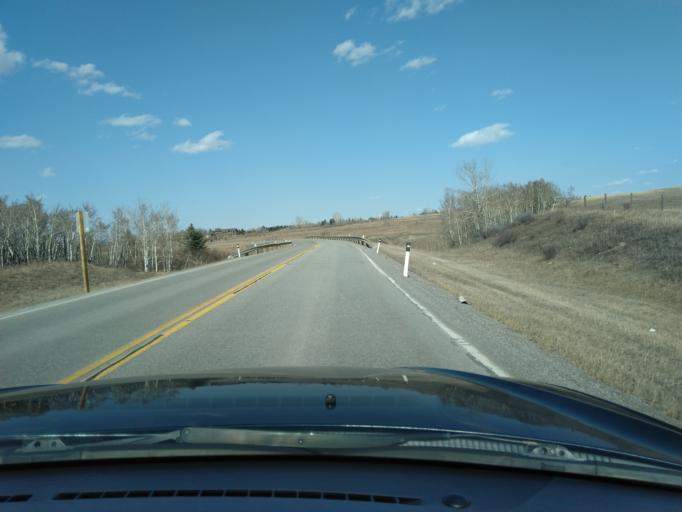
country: CA
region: Alberta
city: Cochrane
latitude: 51.0936
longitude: -114.3022
